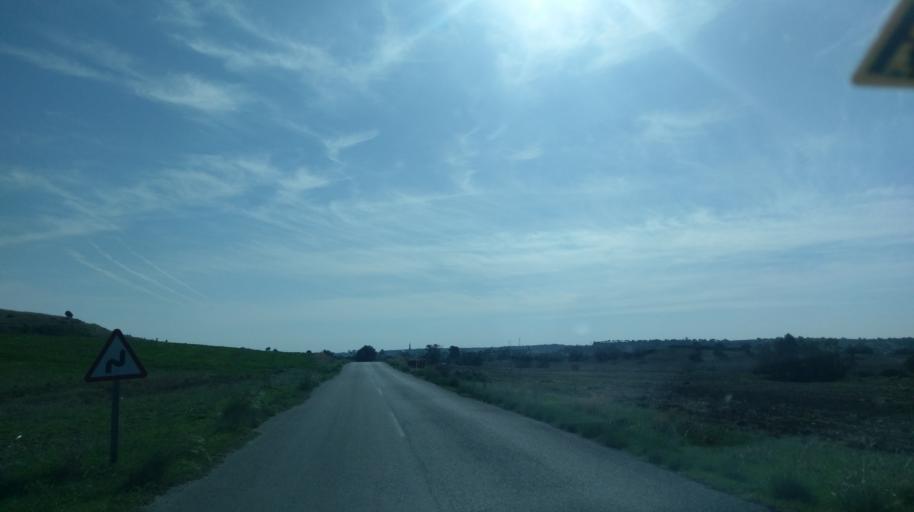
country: CY
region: Ammochostos
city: Trikomo
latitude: 35.3382
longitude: 33.9297
